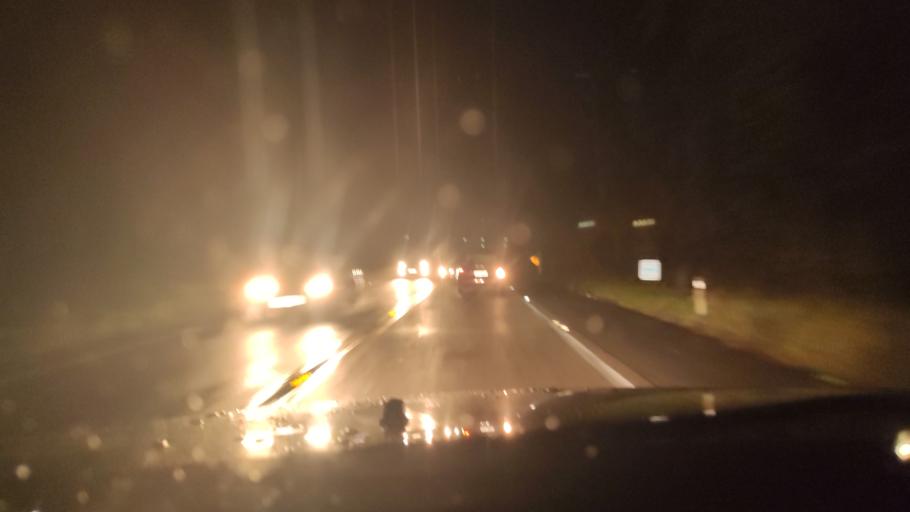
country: BR
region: Sao Paulo
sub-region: Sao Sebastiao
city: Sao Sebastiao
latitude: -23.7357
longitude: -45.4001
